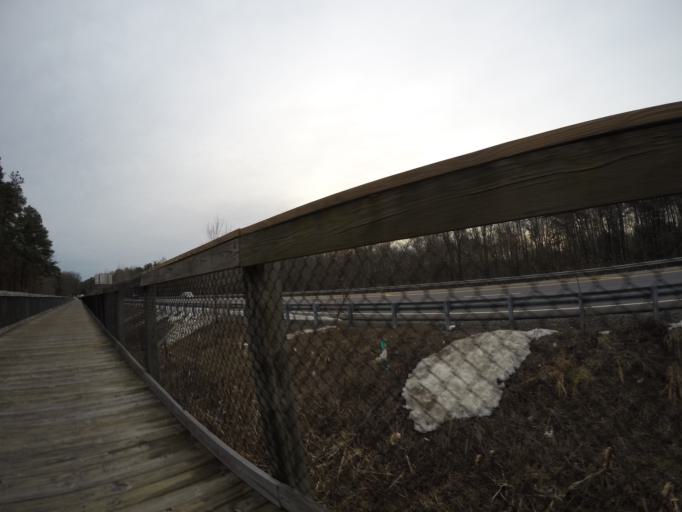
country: US
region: Maryland
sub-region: Anne Arundel County
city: Severn
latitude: 39.1689
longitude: -76.6948
